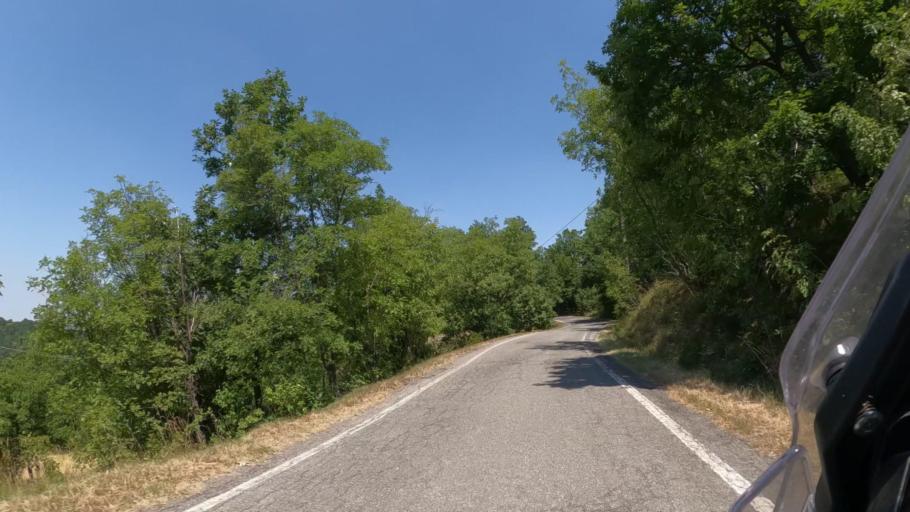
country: IT
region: Piedmont
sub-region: Provincia di Alessandria
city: Morbello
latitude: 44.5637
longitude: 8.5179
